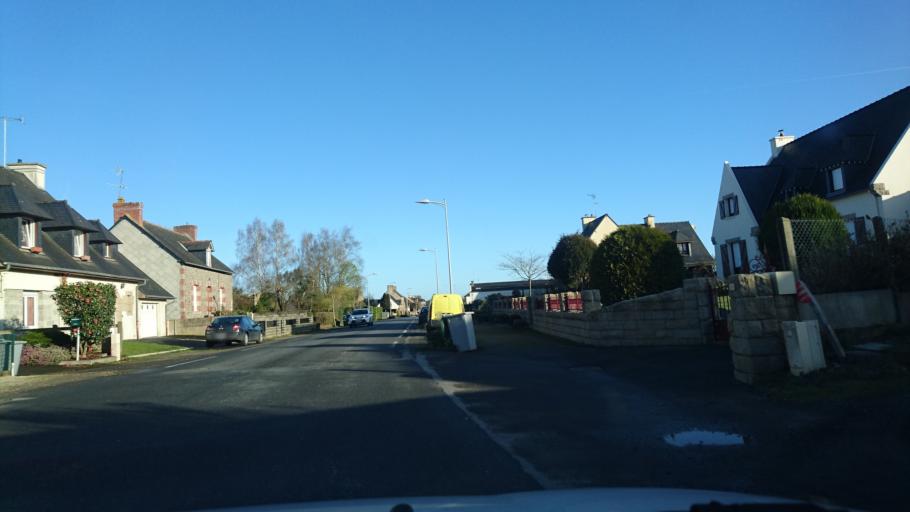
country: FR
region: Brittany
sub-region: Departement d'Ille-et-Vilaine
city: La Boussac
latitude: 48.5133
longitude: -1.6623
